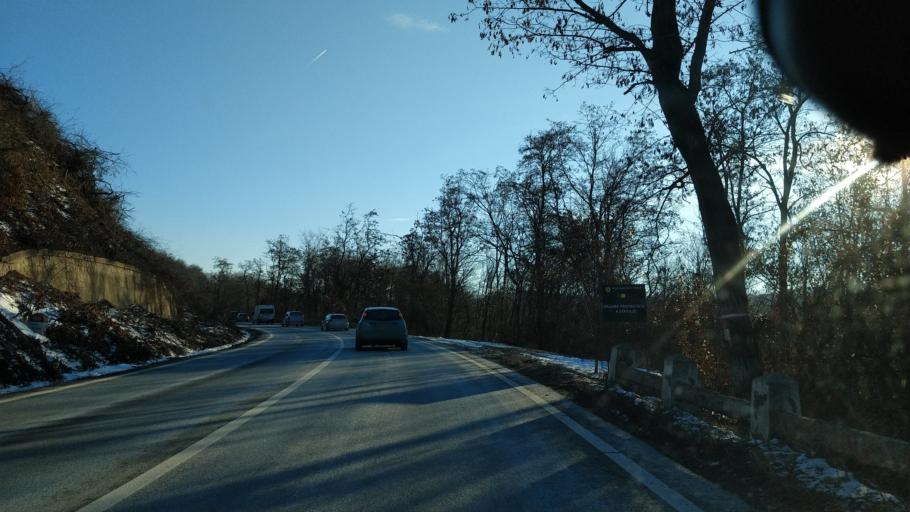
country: RO
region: Bacau
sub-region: Comuna Luizi-Calugara
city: Luizi-Calugara
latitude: 46.5406
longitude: 26.8188
